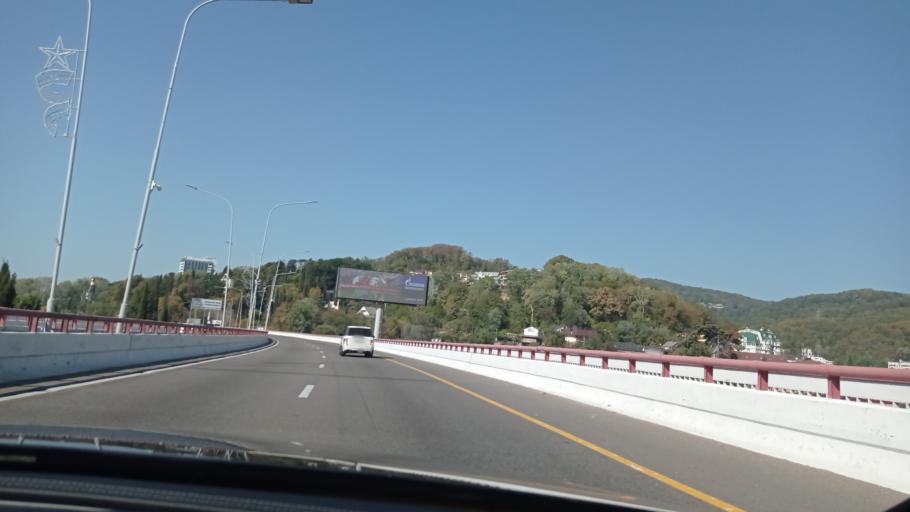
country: RU
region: Krasnodarskiy
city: Kudepsta
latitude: 43.4913
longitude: 39.8890
